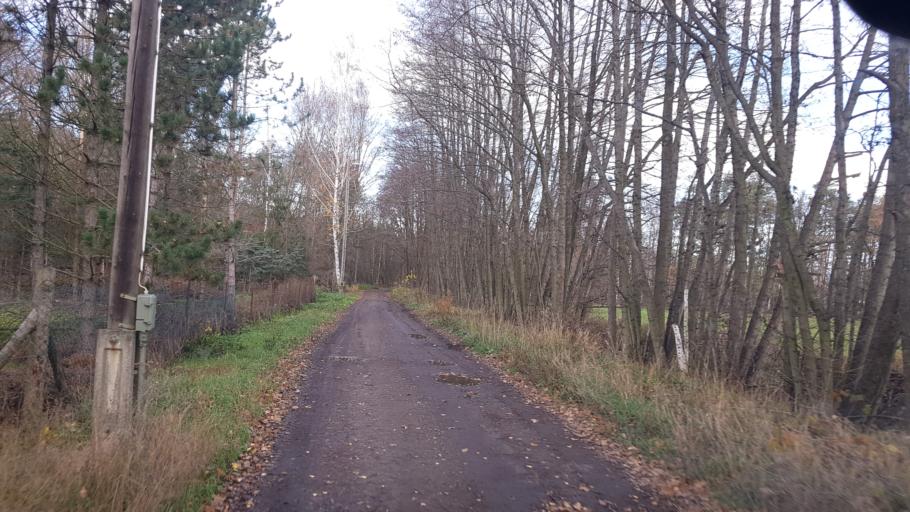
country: DE
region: Brandenburg
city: Falkenberg
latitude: 51.5850
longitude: 13.2761
